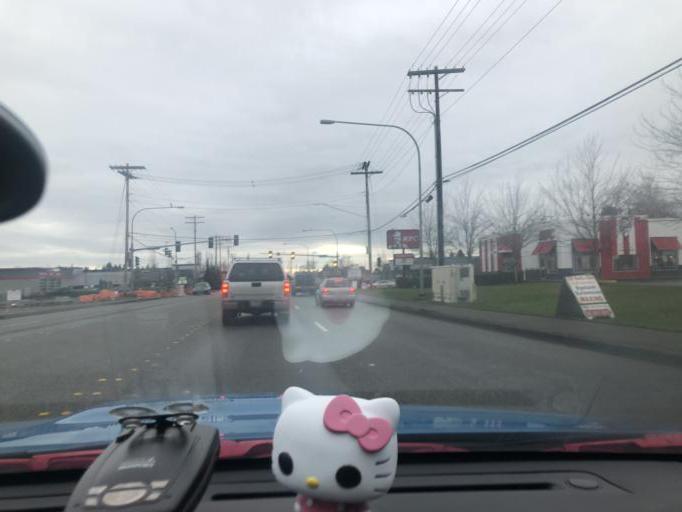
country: US
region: Washington
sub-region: Snohomish County
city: Smokey Point
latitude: 48.1508
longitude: -122.1831
